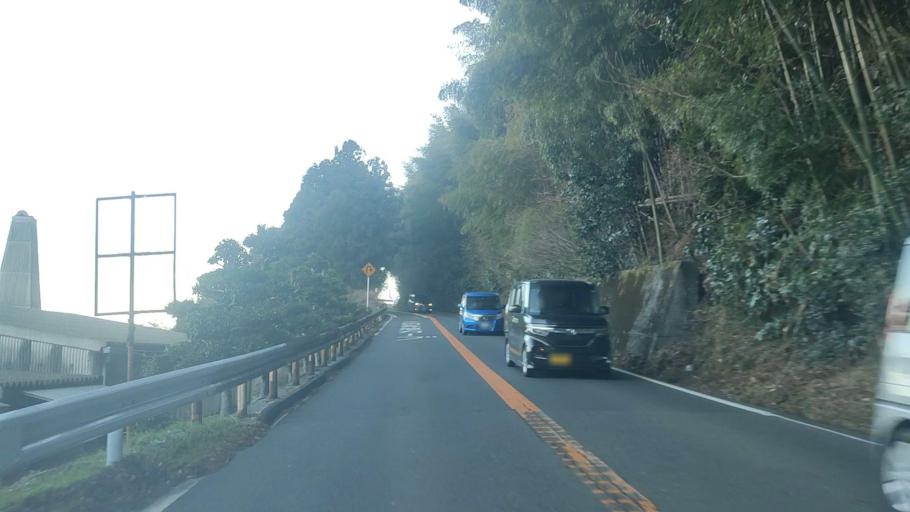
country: JP
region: Oita
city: Beppu
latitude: 33.2885
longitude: 131.4668
